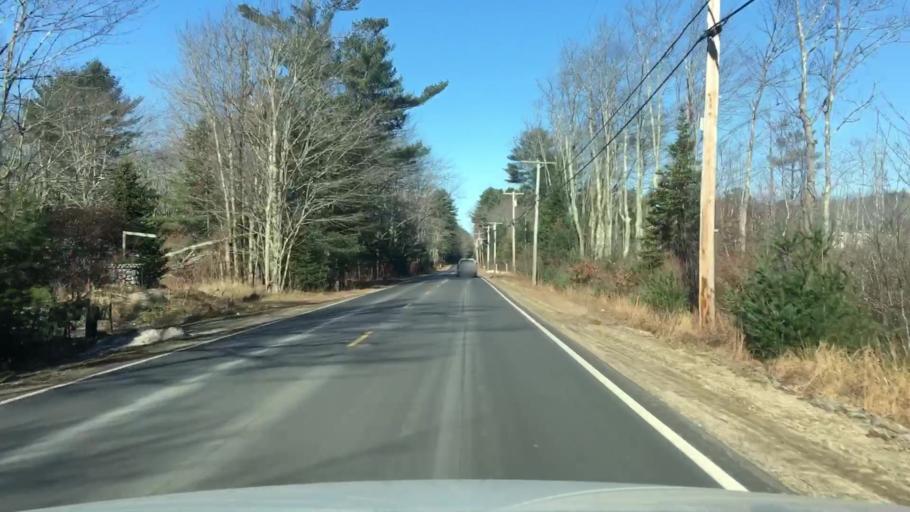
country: US
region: Maine
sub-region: York County
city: Arundel
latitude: 43.3873
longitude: -70.4801
